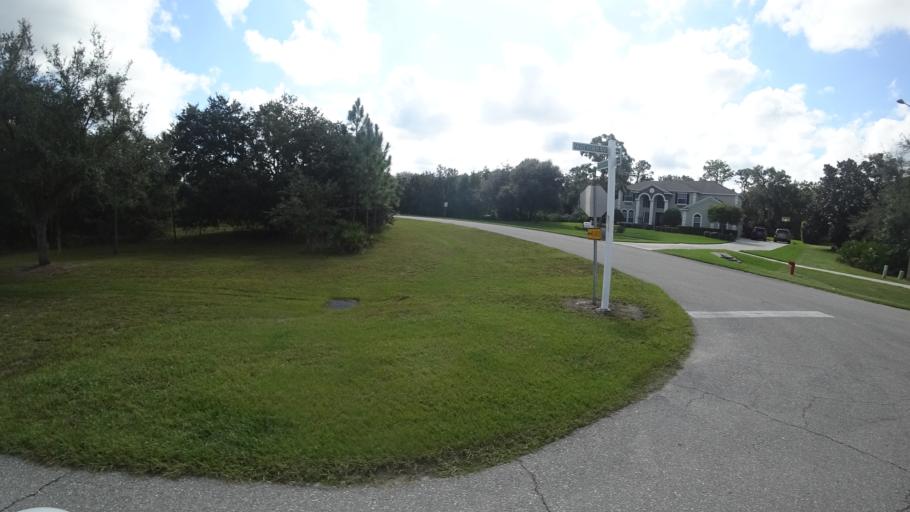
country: US
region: Florida
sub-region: Sarasota County
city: Fruitville
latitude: 27.3903
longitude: -82.3048
